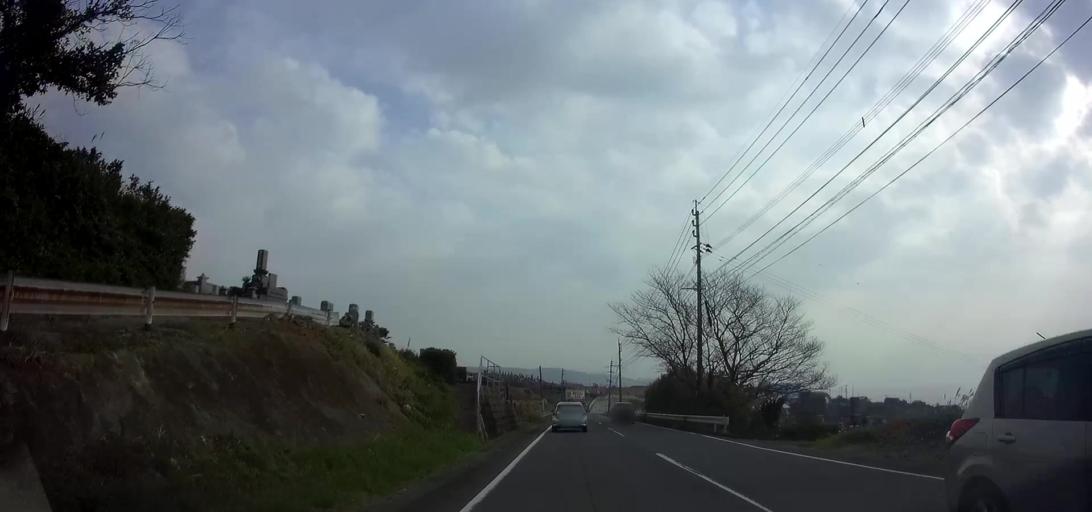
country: JP
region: Nagasaki
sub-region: Isahaya-shi
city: Isahaya
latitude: 32.7914
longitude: 130.0618
